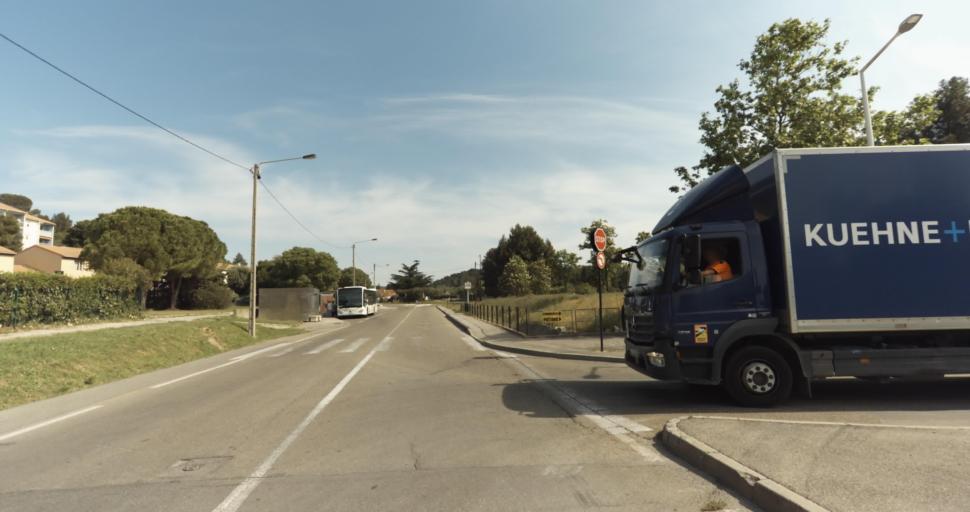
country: FR
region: Languedoc-Roussillon
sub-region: Departement du Gard
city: Marguerittes
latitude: 43.8593
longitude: 4.4024
